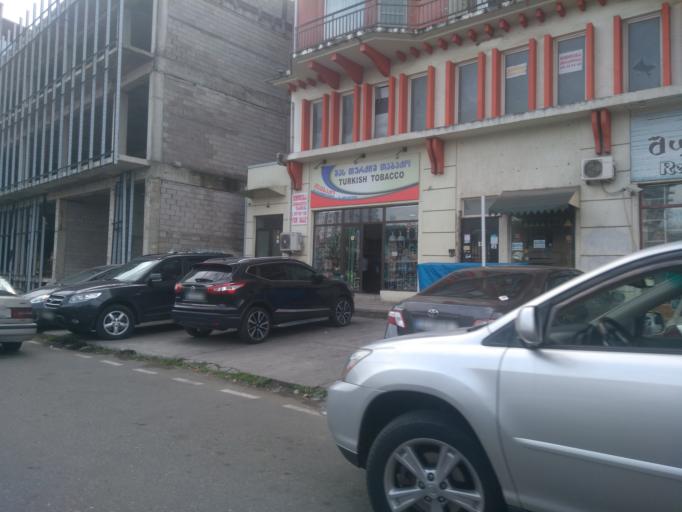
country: GE
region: Ajaria
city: Batumi
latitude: 41.6441
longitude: 41.6423
